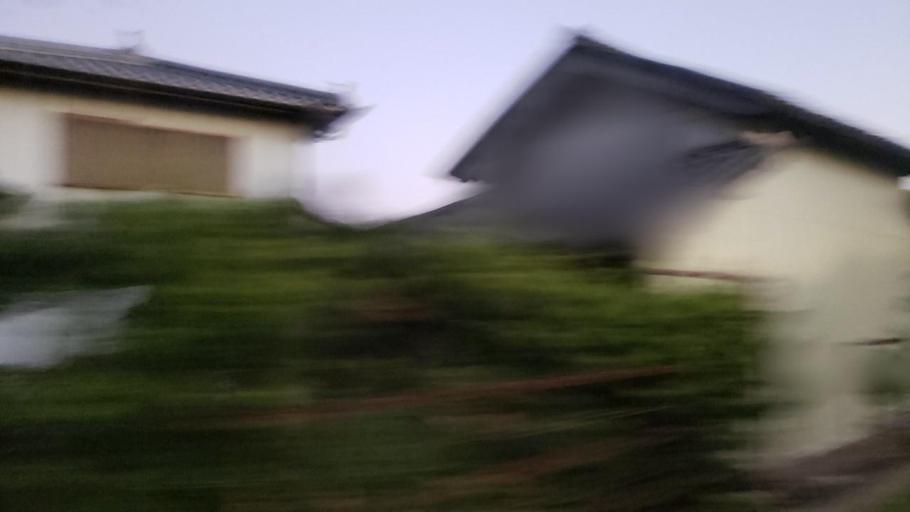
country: JP
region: Tokushima
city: Kamojimacho-jogejima
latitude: 34.1002
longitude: 134.2985
